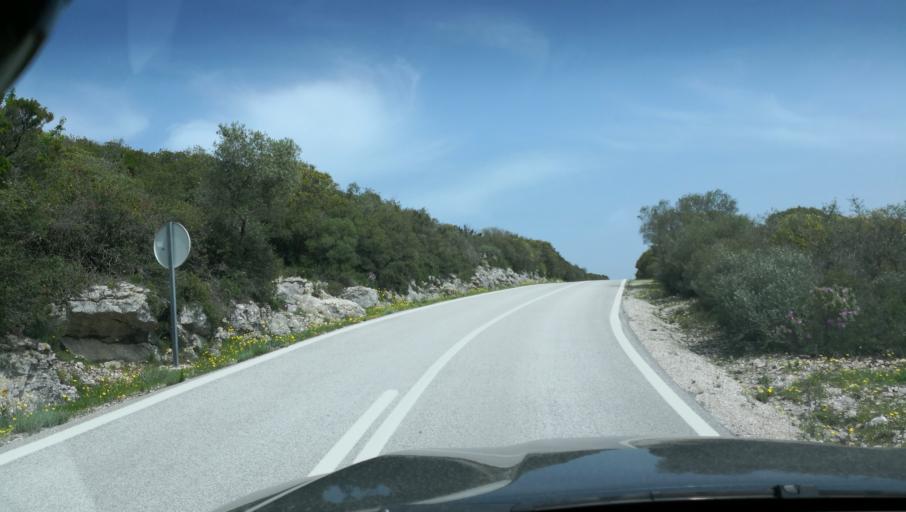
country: PT
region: Setubal
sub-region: Palmela
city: Quinta do Anjo
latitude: 38.4867
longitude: -8.9875
